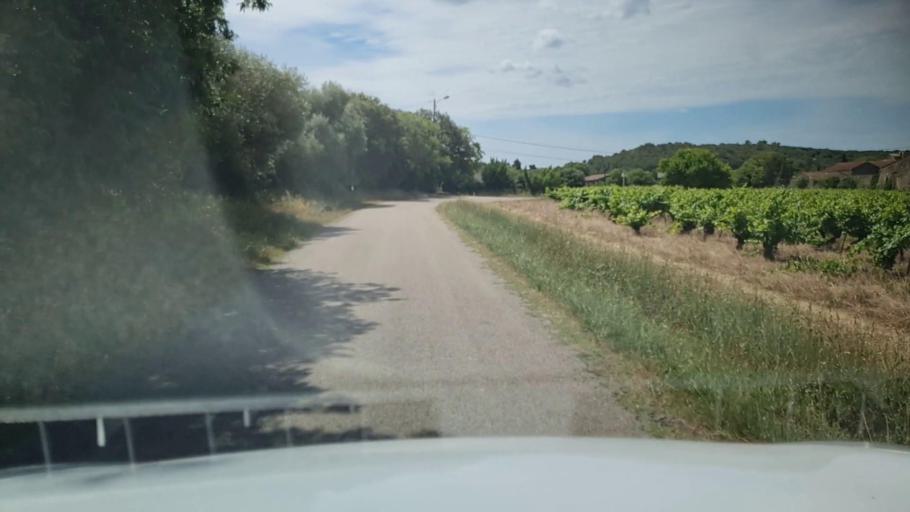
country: FR
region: Languedoc-Roussillon
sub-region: Departement du Gard
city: Congenies
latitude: 43.8214
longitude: 4.1478
